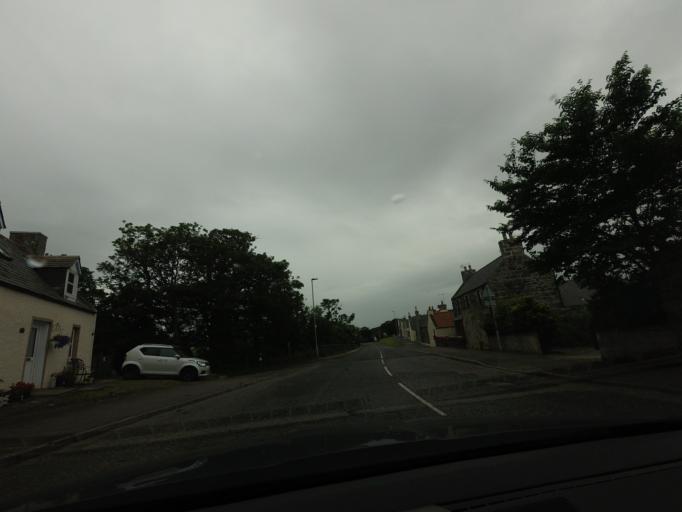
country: GB
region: Scotland
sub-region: Aberdeenshire
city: Portsoy
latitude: 57.6811
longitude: -2.6868
